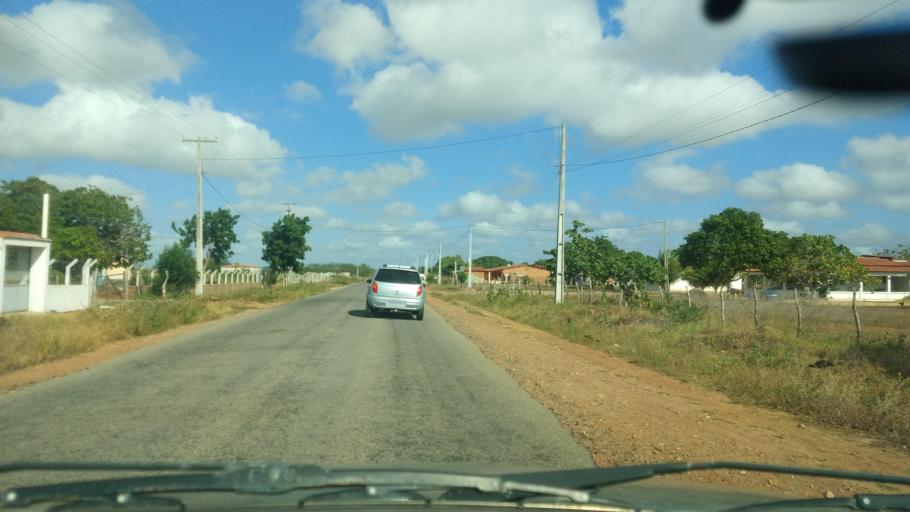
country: BR
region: Rio Grande do Norte
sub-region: Sao Paulo Do Potengi
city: Sao Paulo do Potengi
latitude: -5.9161
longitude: -35.7189
